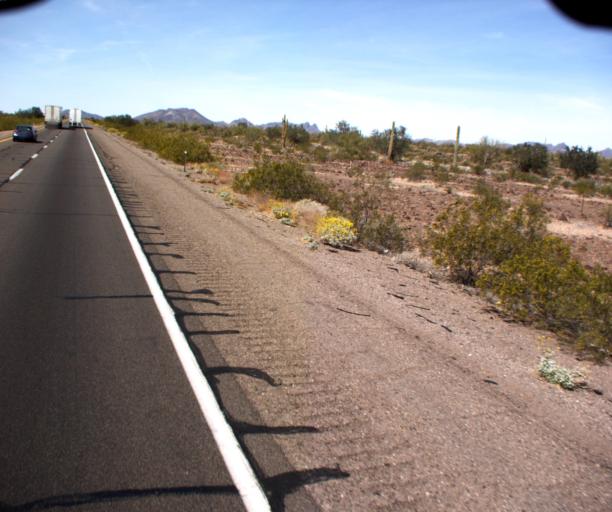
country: US
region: Arizona
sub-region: La Paz County
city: Quartzsite
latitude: 33.6514
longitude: -113.9223
